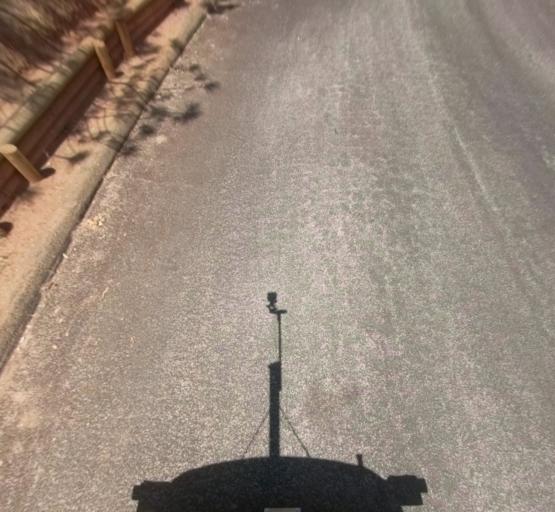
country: US
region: California
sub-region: Fresno County
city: Auberry
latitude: 37.2275
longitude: -119.4685
